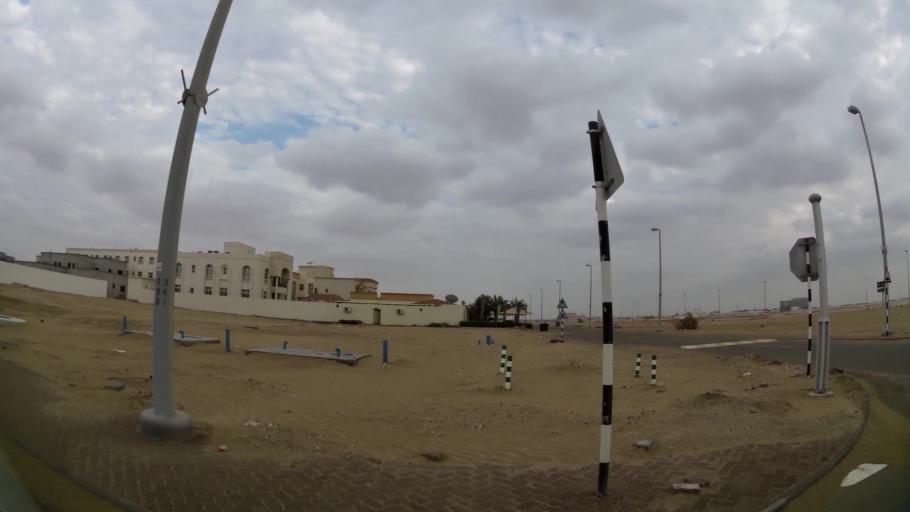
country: AE
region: Abu Dhabi
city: Abu Dhabi
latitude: 24.3485
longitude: 54.6081
